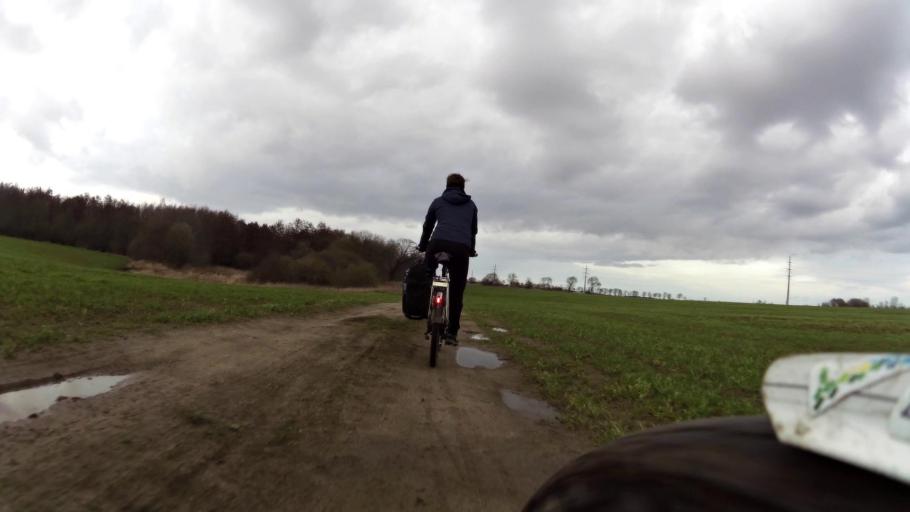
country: PL
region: West Pomeranian Voivodeship
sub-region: Powiat kamienski
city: Kamien Pomorski
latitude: 53.9442
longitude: 14.7687
